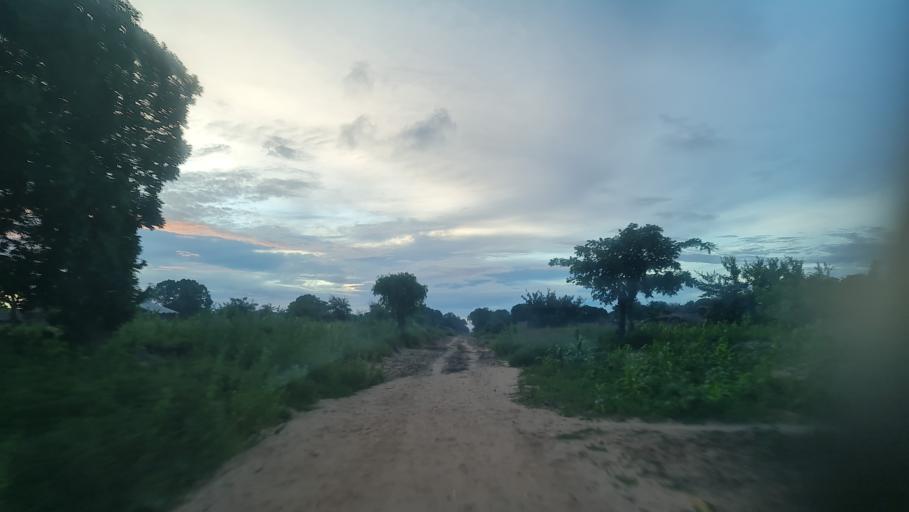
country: MZ
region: Nampula
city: Nampula
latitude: -14.7365
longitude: 39.9244
